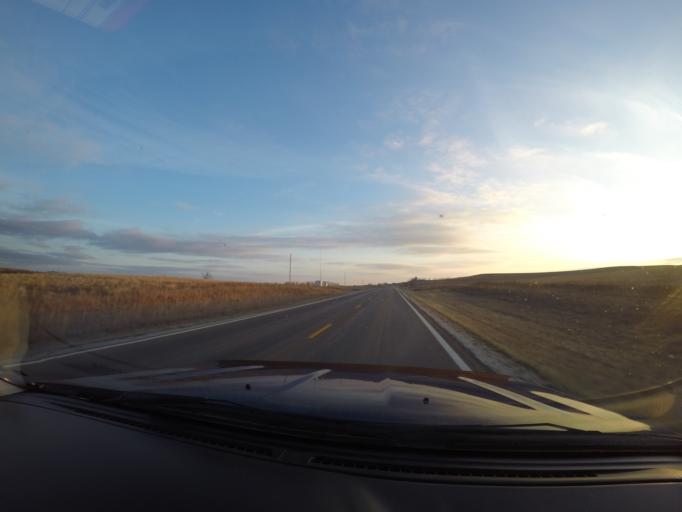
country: US
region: Kansas
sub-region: Chase County
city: Cottonwood Falls
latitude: 38.4159
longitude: -96.5572
